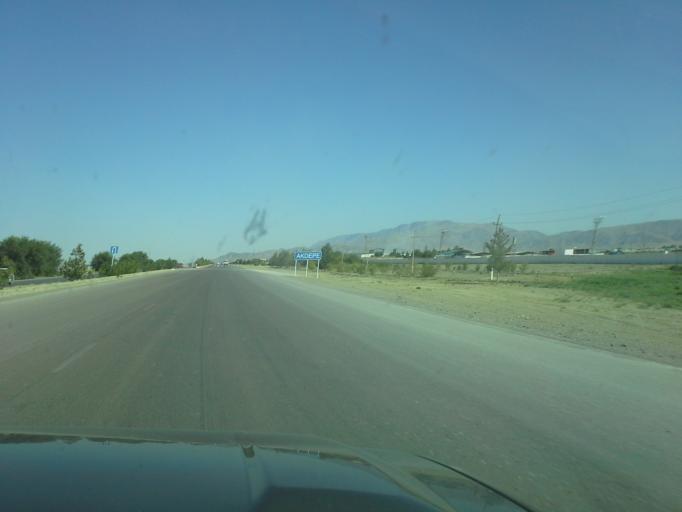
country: TM
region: Ahal
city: Baharly
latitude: 38.3260
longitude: 57.5874
